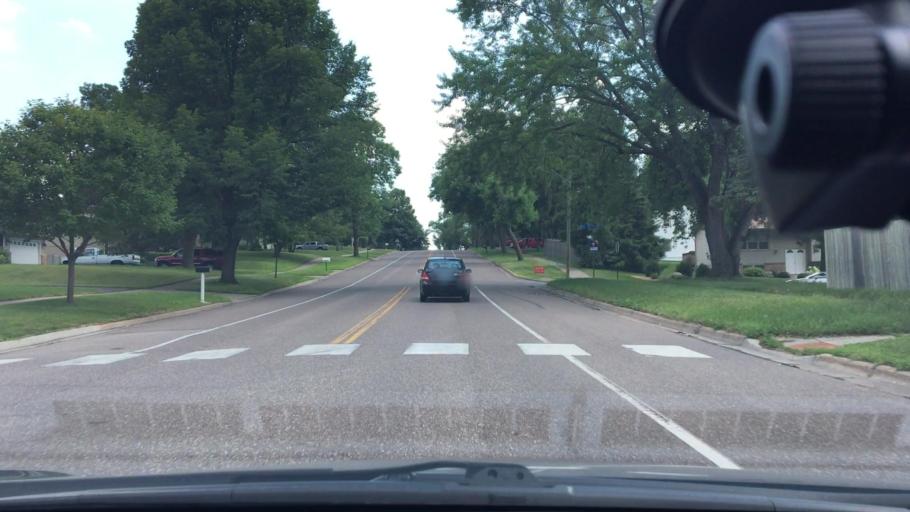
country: US
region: Minnesota
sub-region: Hennepin County
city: New Hope
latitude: 45.0402
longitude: -93.3905
